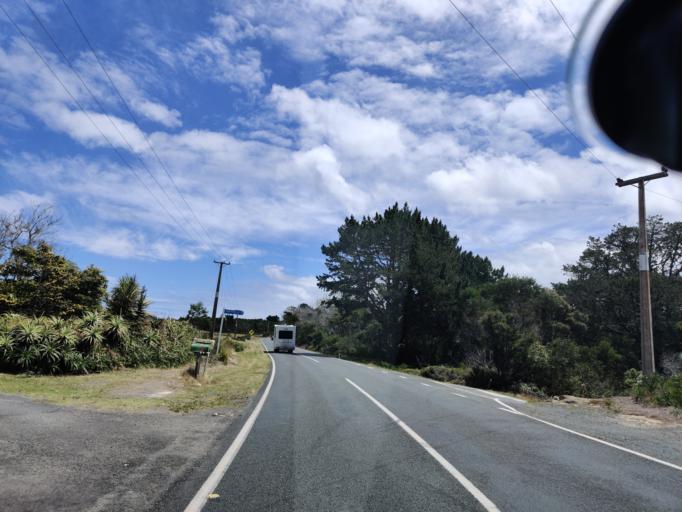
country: NZ
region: Northland
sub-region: Far North District
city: Kaitaia
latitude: -34.7851
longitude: 173.0988
